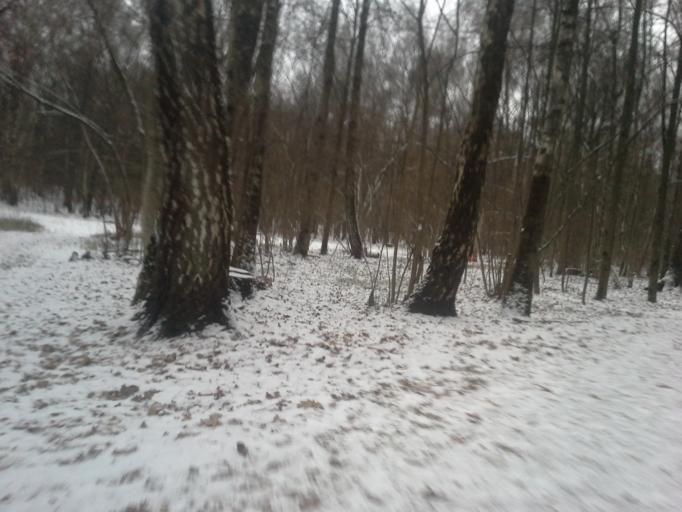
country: RU
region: Moscow
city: Chertanovo Yuzhnoye
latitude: 55.6153
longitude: 37.5723
